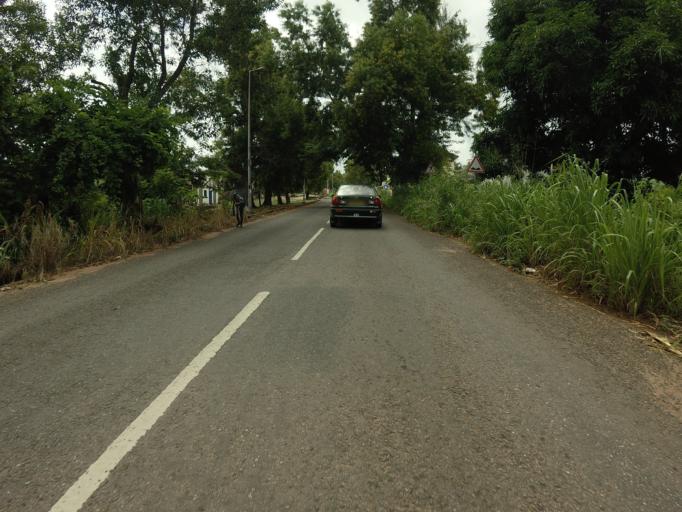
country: GH
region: Volta
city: Ho
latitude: 6.5988
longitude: 0.4626
